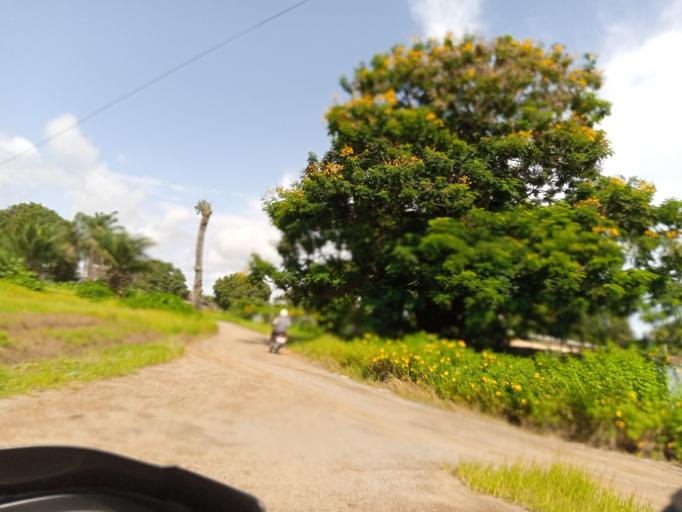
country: SL
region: Northern Province
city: Tintafor
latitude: 8.6157
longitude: -13.2090
